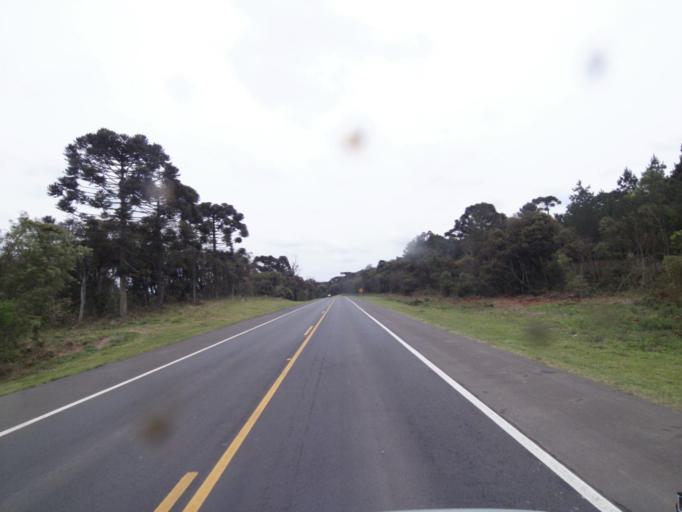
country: BR
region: Parana
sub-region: Irati
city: Irati
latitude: -25.4672
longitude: -50.5103
